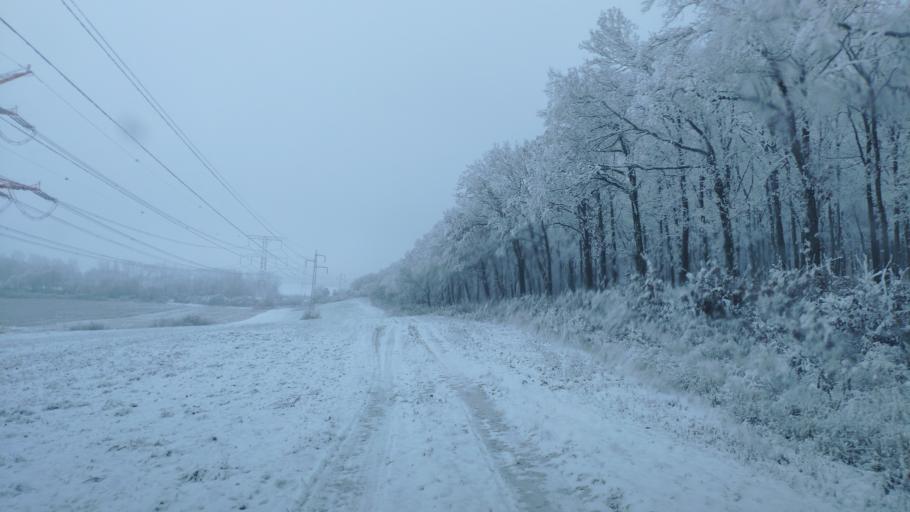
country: SK
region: Kosicky
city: Kosice
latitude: 48.6456
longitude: 21.1735
